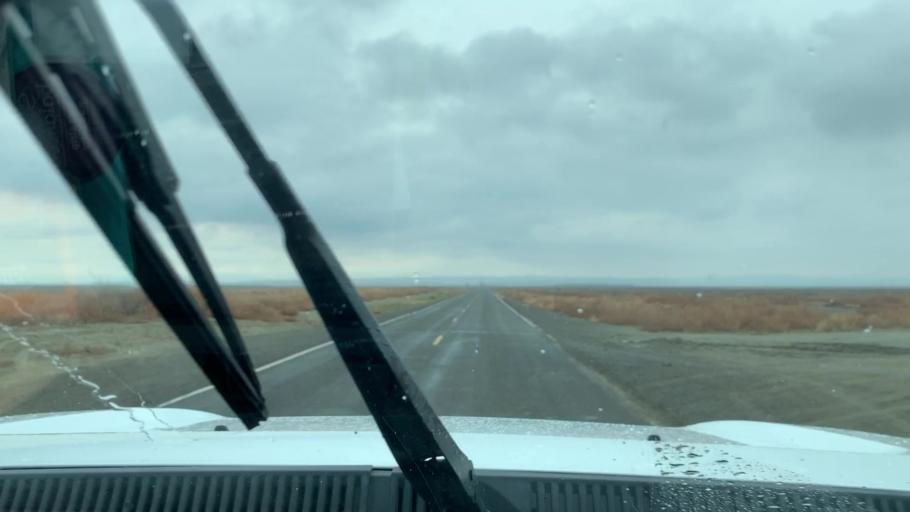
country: US
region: California
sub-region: Kings County
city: Kettleman City
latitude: 35.9340
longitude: -119.8255
